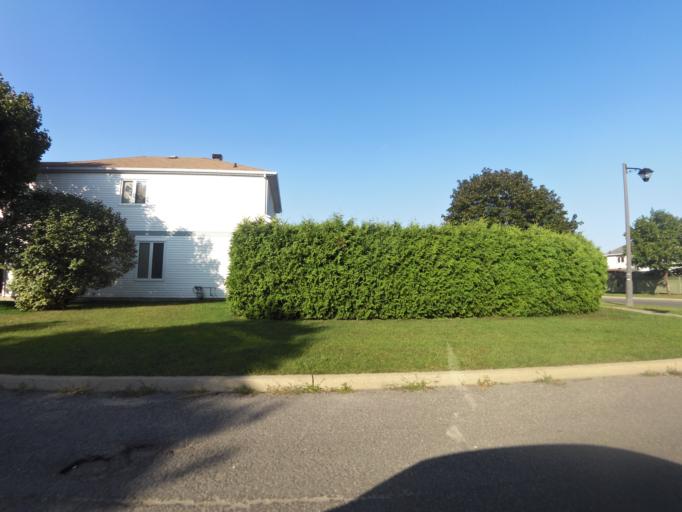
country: CA
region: Ontario
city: Clarence-Rockland
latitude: 45.4791
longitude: -75.4783
